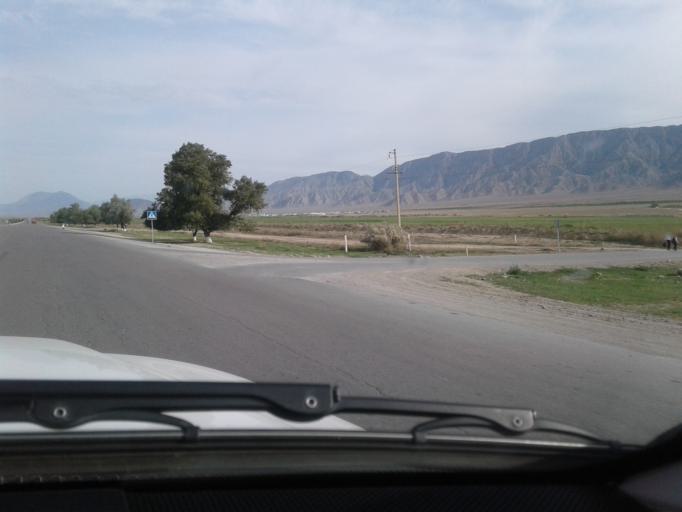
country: TM
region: Ahal
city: Arcabil
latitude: 38.2061
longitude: 57.8195
